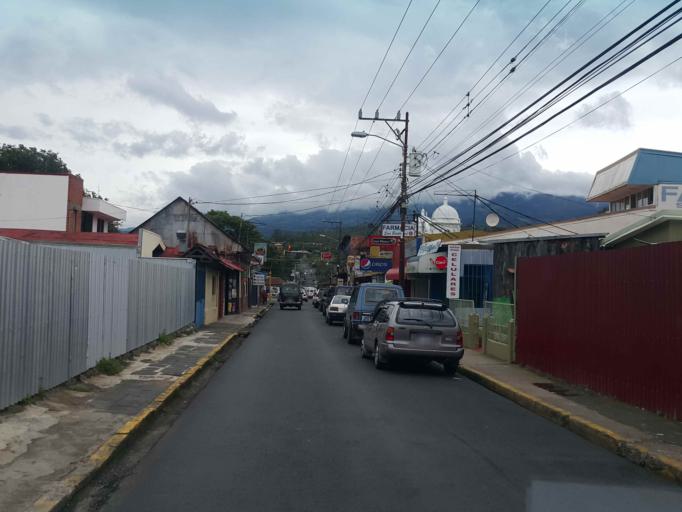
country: CR
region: Heredia
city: Mercedes
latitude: 10.0196
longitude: -84.1236
